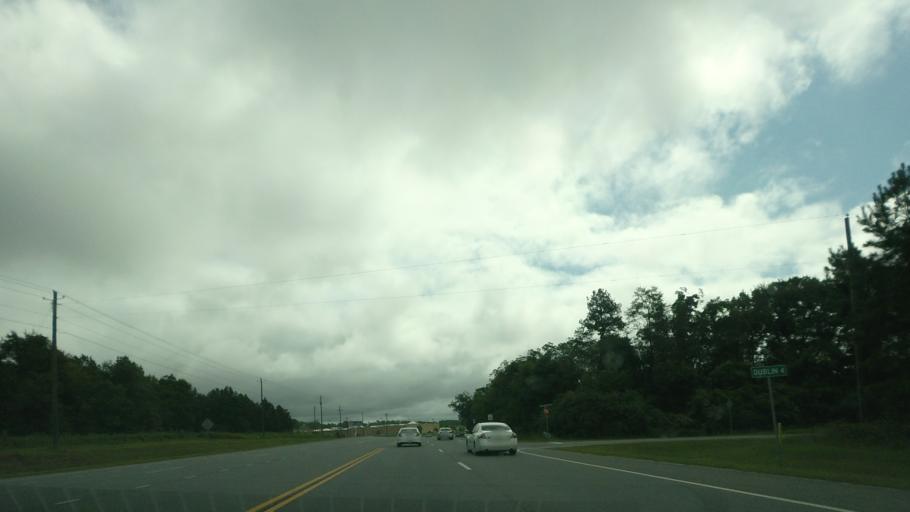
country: US
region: Georgia
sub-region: Laurens County
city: Dublin
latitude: 32.5507
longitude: -82.9772
